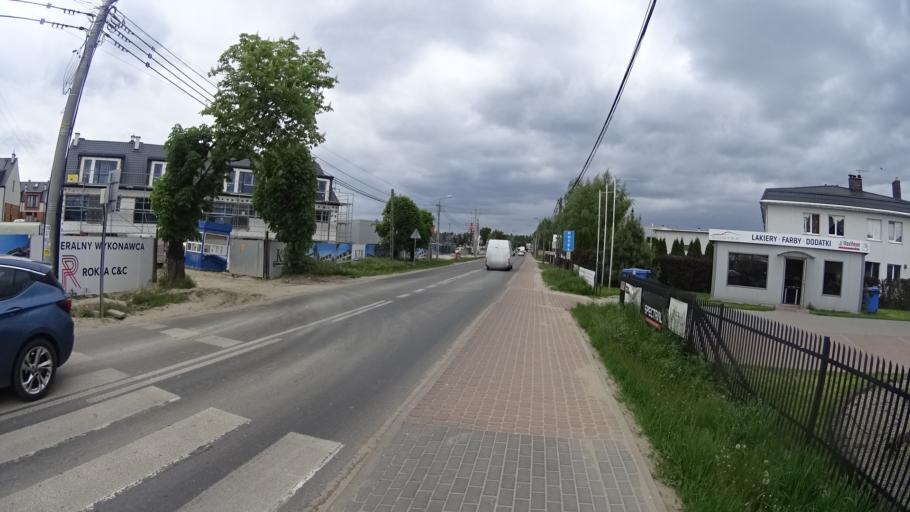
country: PL
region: Masovian Voivodeship
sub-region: Powiat warszawski zachodni
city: Babice
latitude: 52.2455
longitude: 20.8487
